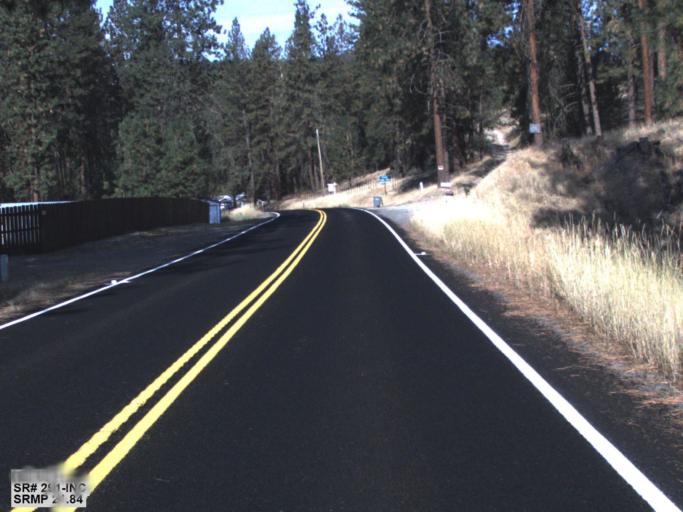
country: US
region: Washington
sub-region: Spokane County
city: Deer Park
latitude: 47.8917
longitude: -117.6765
